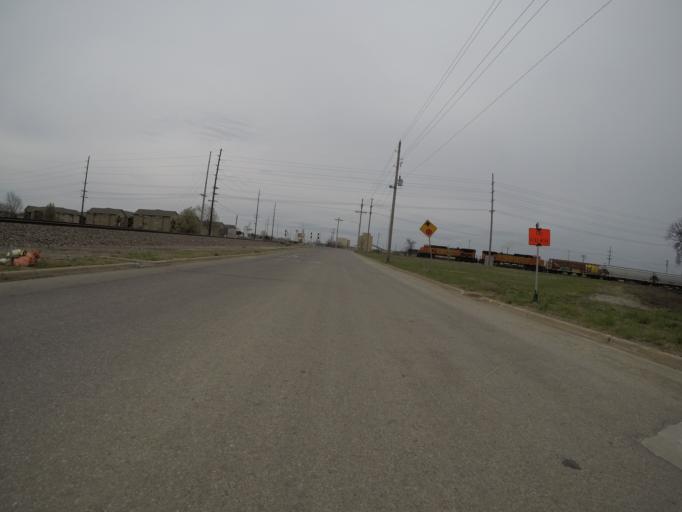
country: US
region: Kansas
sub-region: Johnson County
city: Olathe
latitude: 38.8700
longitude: -94.8069
